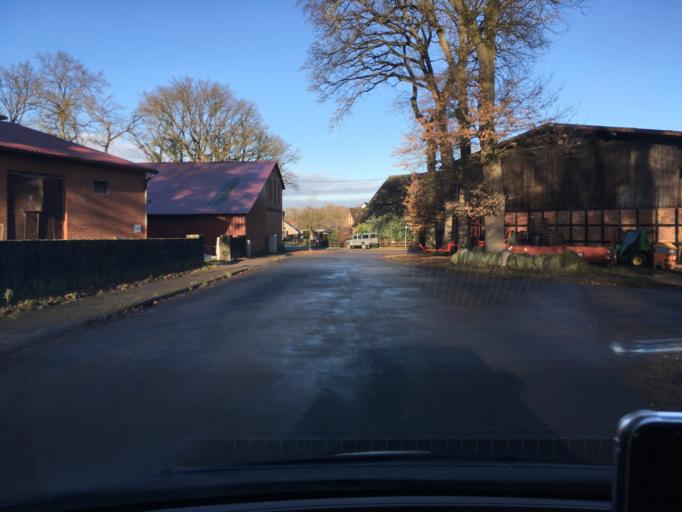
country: DE
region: Lower Saxony
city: Wendisch Evern
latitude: 53.2144
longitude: 10.4724
